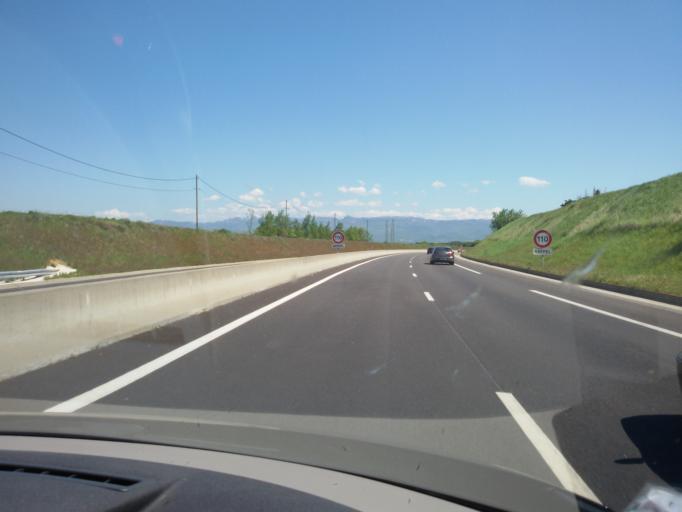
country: FR
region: Rhone-Alpes
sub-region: Departement de la Drome
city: Bourg-les-Valence
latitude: 44.9647
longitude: 4.9160
